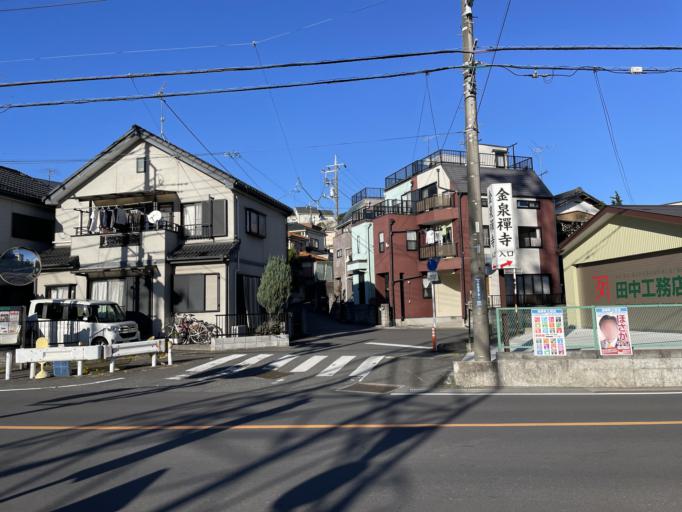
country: JP
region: Saitama
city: Wako
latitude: 35.7942
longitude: 139.6273
